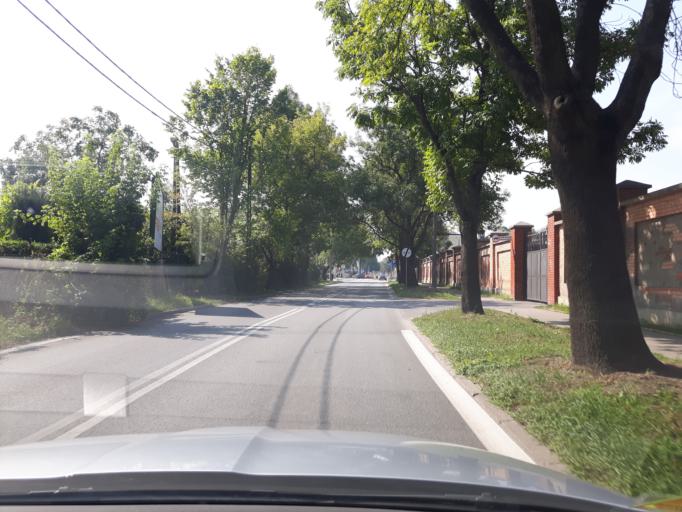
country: PL
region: Masovian Voivodeship
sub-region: Warszawa
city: Targowek
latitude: 52.2797
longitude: 21.0455
